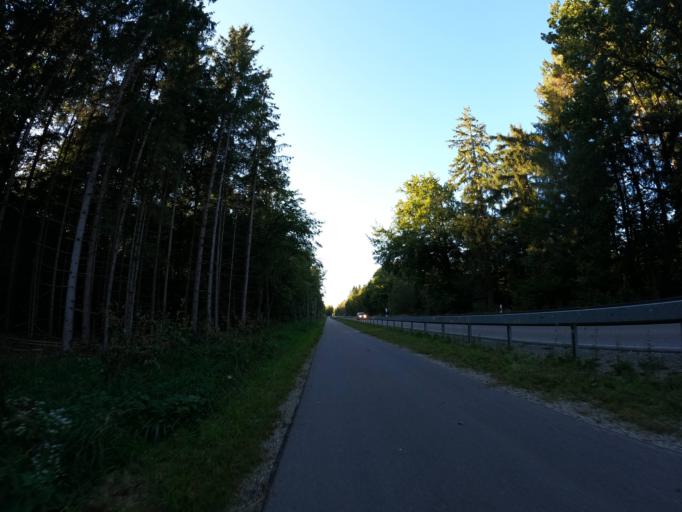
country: DE
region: Bavaria
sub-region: Upper Bavaria
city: Grasbrunn
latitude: 48.0582
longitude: 11.7535
